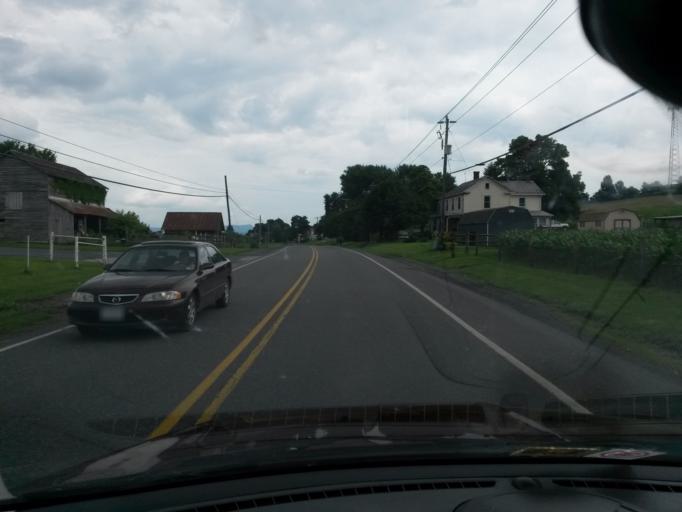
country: US
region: Virginia
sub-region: Rockingham County
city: Dayton
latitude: 38.4593
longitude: -78.9565
